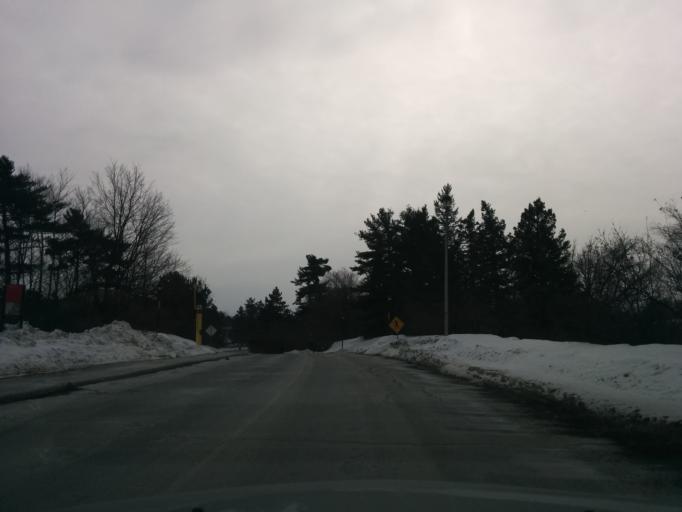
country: CA
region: Ontario
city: Ottawa
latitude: 45.3806
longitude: -75.7010
